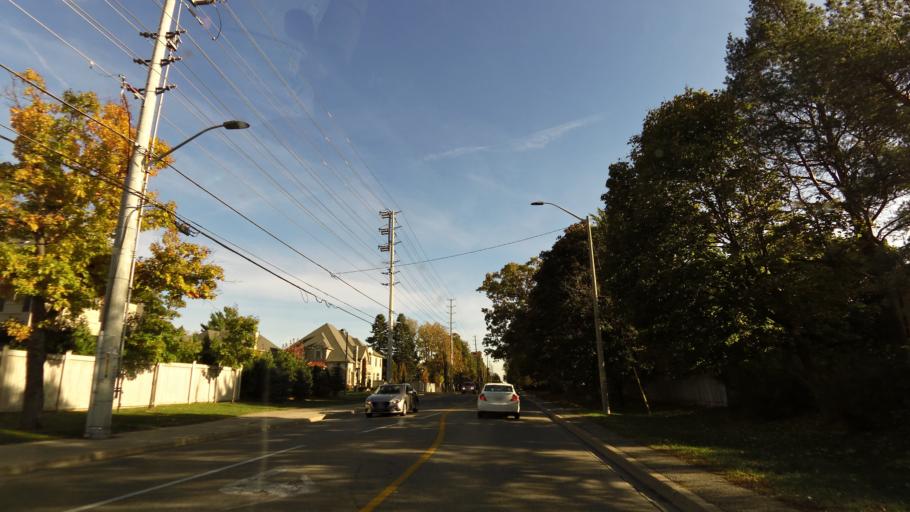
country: CA
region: Ontario
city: Mississauga
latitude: 43.5516
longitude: -79.6728
